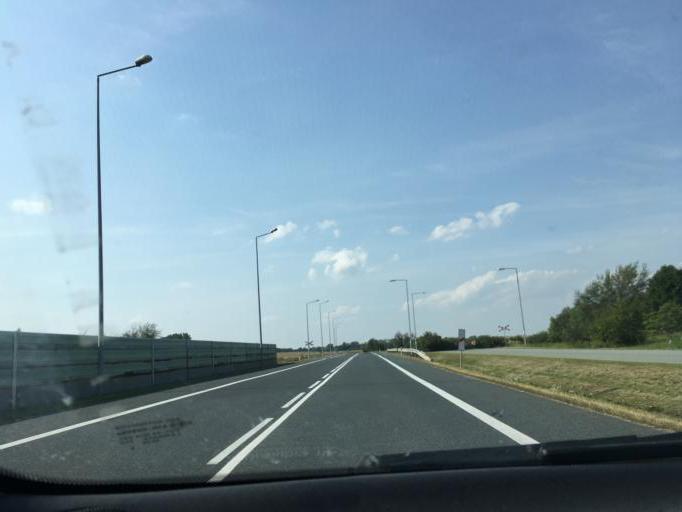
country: PL
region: Opole Voivodeship
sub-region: Powiat prudnicki
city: Prudnik
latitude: 50.3311
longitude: 17.5980
